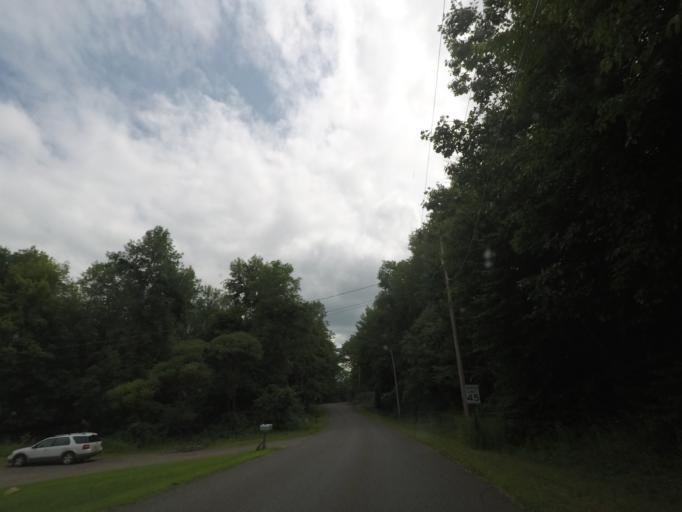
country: US
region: New York
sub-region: Saratoga County
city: Stillwater
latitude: 43.0002
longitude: -73.6869
